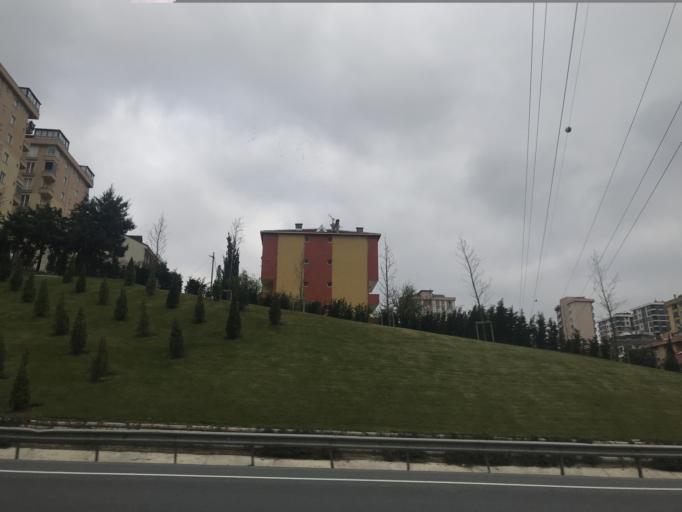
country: TR
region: Istanbul
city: Umraniye
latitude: 41.0049
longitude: 29.1214
